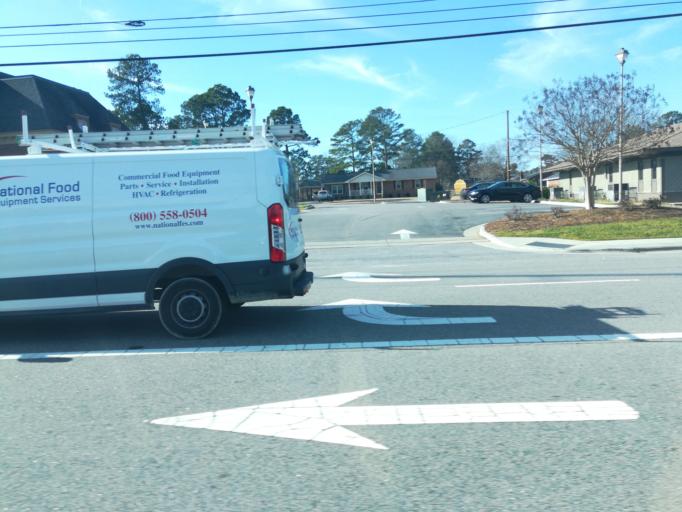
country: US
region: North Carolina
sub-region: Nash County
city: Rocky Mount
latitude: 35.9644
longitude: -77.8496
